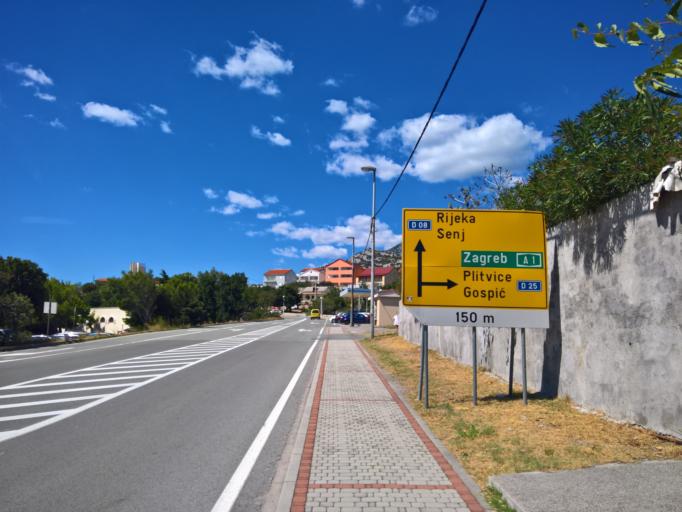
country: HR
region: Licko-Senjska
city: Karlobag
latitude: 44.5289
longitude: 15.0703
